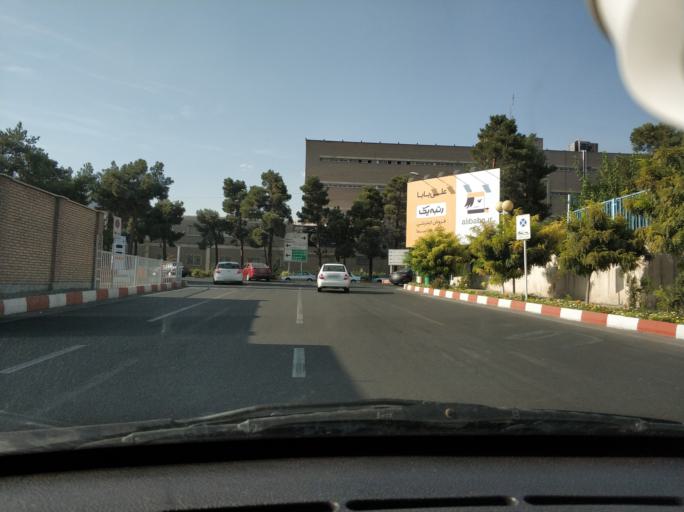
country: IR
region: Tehran
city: Tehran
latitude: 35.6956
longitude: 51.3294
